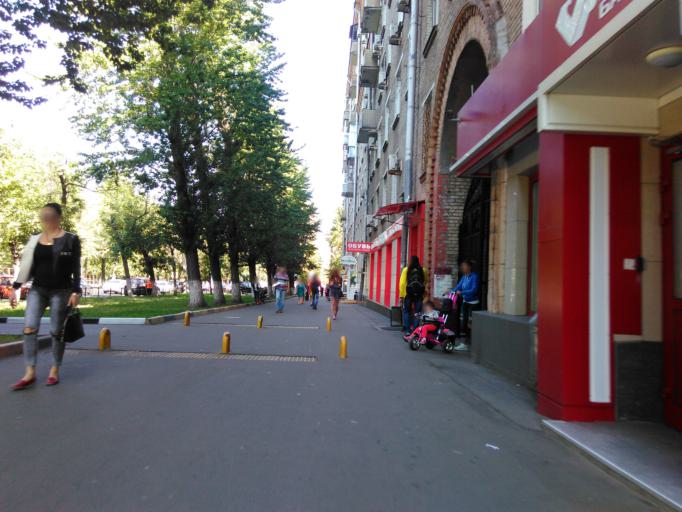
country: RU
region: Moskovskaya
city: Leninskiye Gory
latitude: 55.6845
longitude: 37.5705
